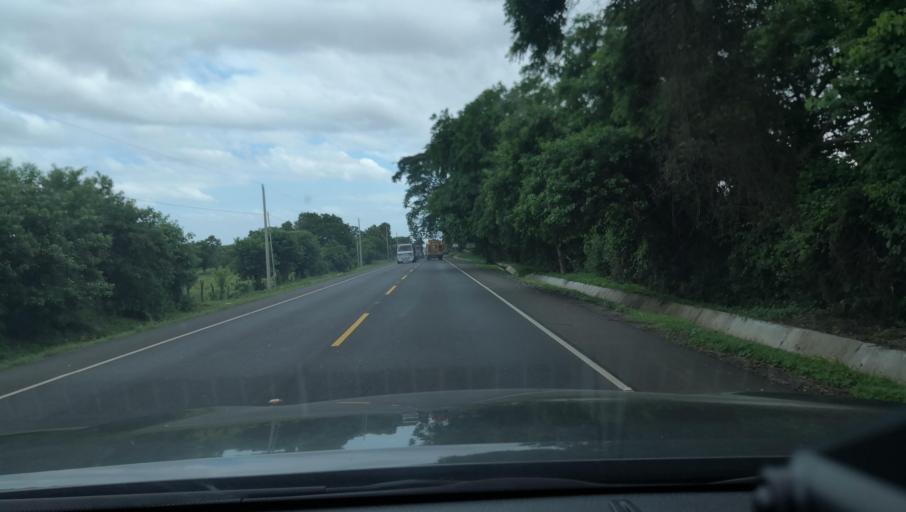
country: NI
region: Masaya
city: Nindiri
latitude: 12.0462
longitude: -86.1320
